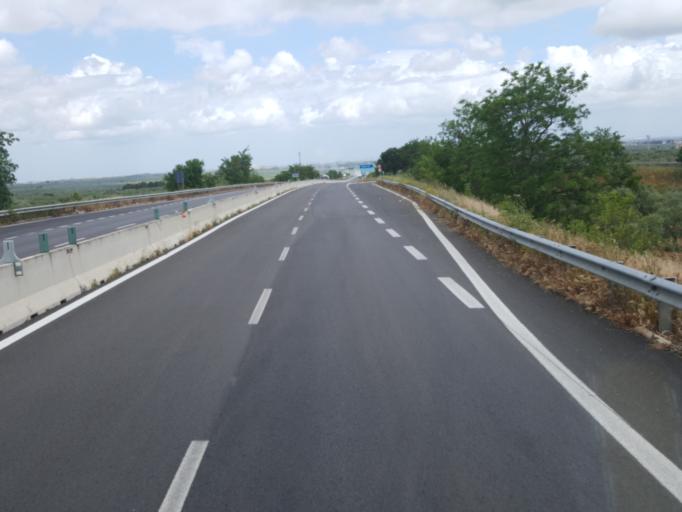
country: IT
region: Apulia
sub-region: Provincia di Bari
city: Toritto
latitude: 40.9956
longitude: 16.6624
